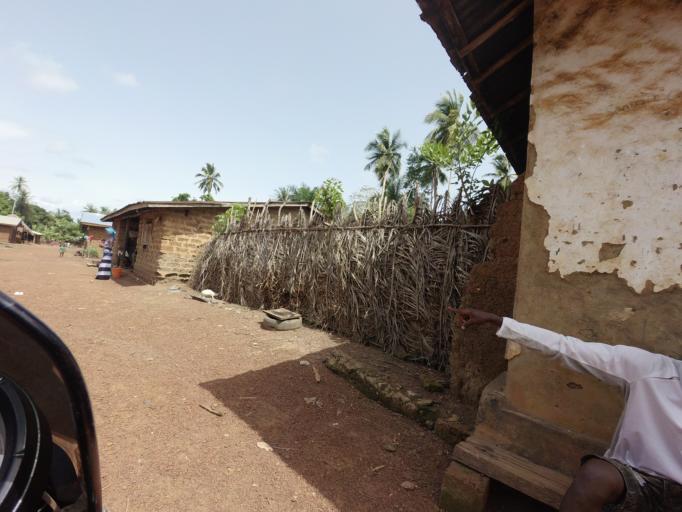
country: SL
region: Northern Province
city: Kambia
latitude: 9.0572
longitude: -12.9728
